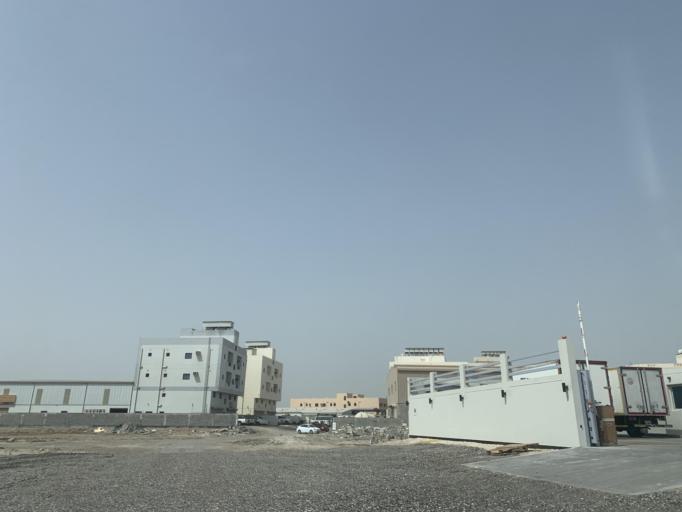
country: BH
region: Northern
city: Madinat `Isa
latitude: 26.1876
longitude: 50.5232
